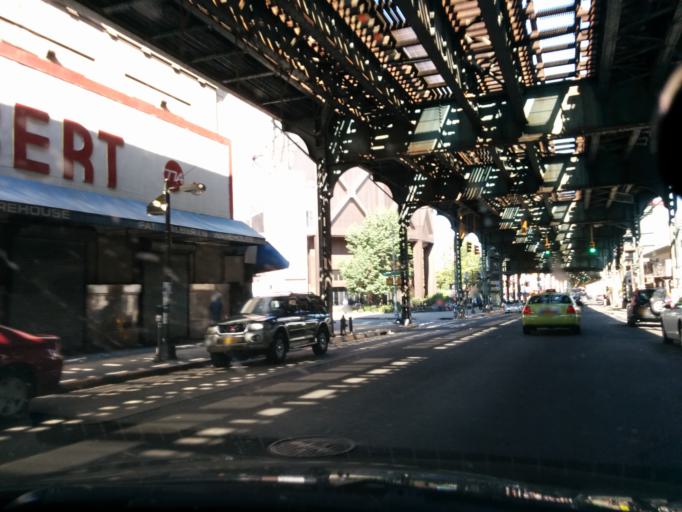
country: US
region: New York
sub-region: Queens County
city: Long Island City
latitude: 40.7001
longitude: -73.9406
